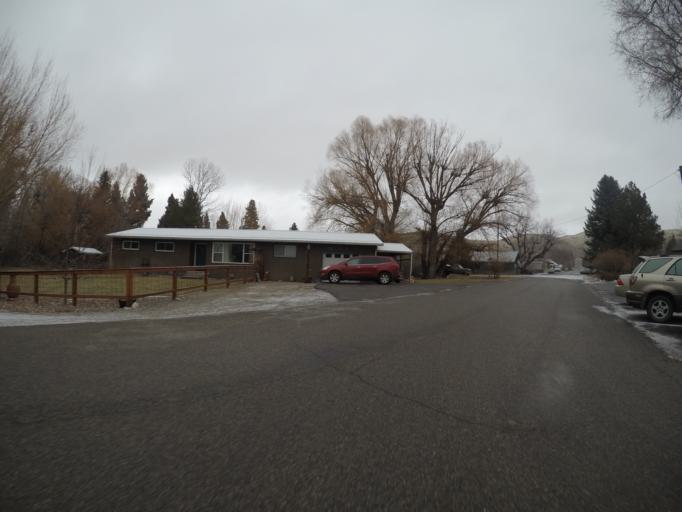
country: US
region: Montana
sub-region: Stillwater County
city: Absarokee
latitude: 45.5198
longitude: -109.4454
